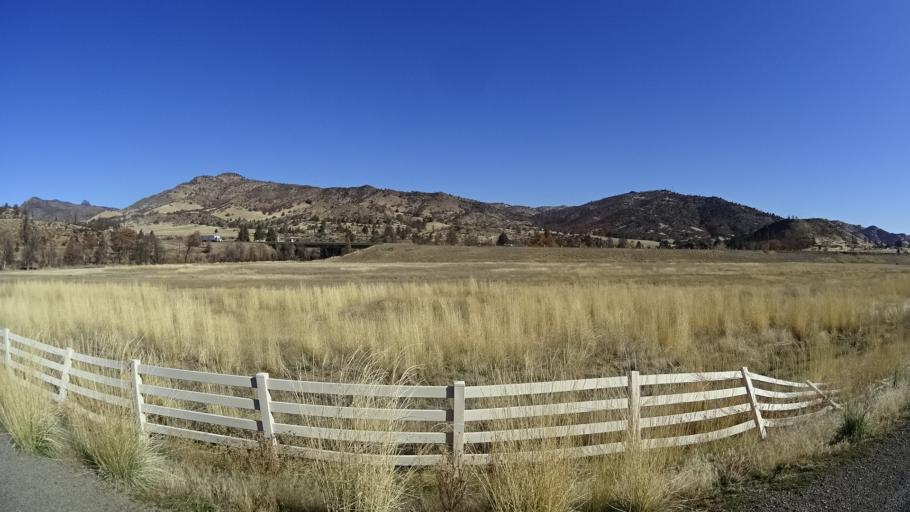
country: US
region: California
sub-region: Siskiyou County
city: Yreka
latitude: 41.9292
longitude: -122.5842
